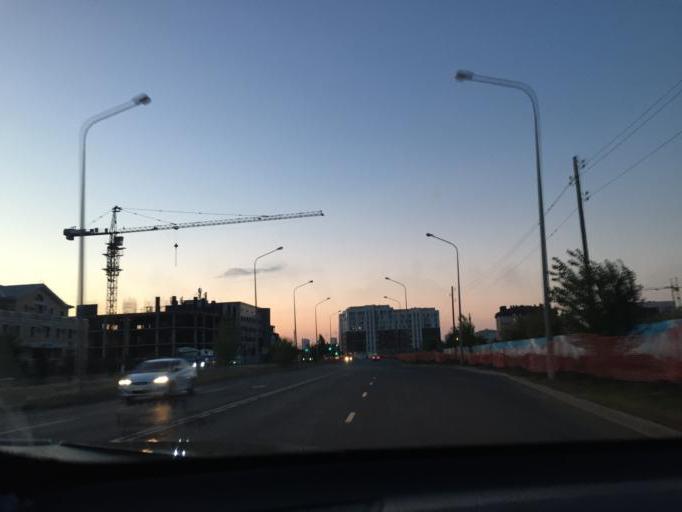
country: KZ
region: Astana Qalasy
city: Astana
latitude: 51.1402
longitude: 71.4569
